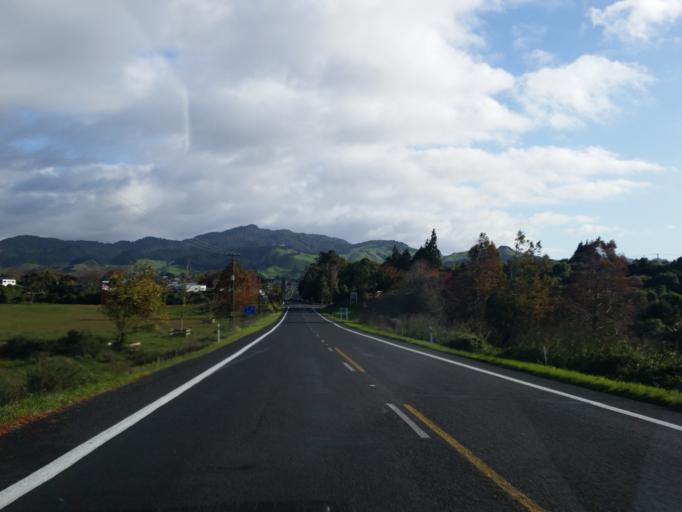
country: NZ
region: Waikato
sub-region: Hauraki District
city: Waihi
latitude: -37.3987
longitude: 175.8524
